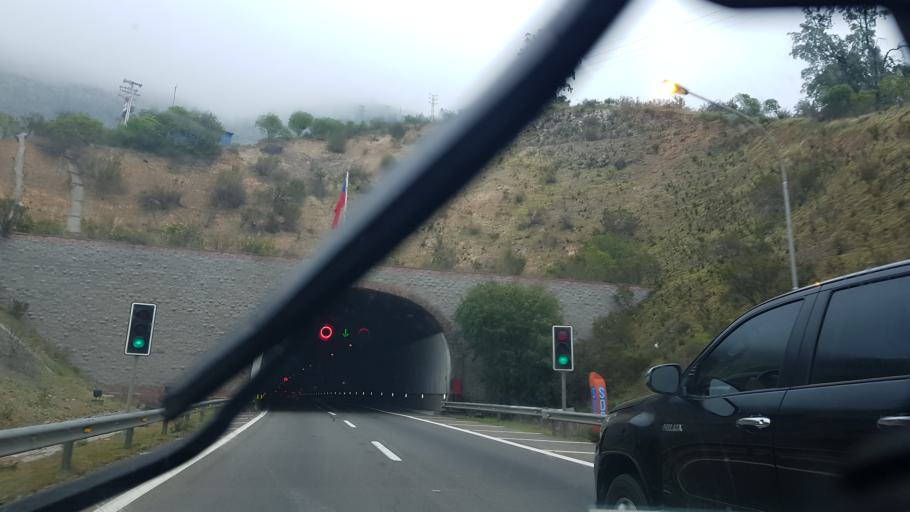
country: CL
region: Santiago Metropolitan
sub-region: Provincia de Talagante
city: Penaflor
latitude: -33.4566
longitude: -70.9337
